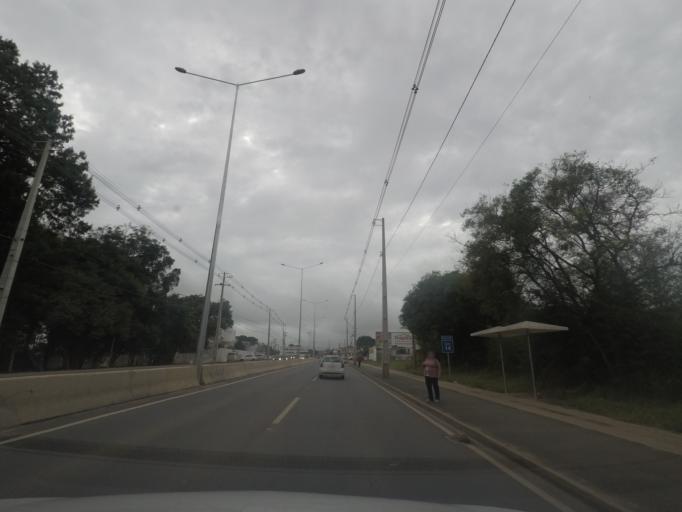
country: BR
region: Parana
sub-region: Piraquara
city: Piraquara
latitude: -25.4544
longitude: -49.0734
